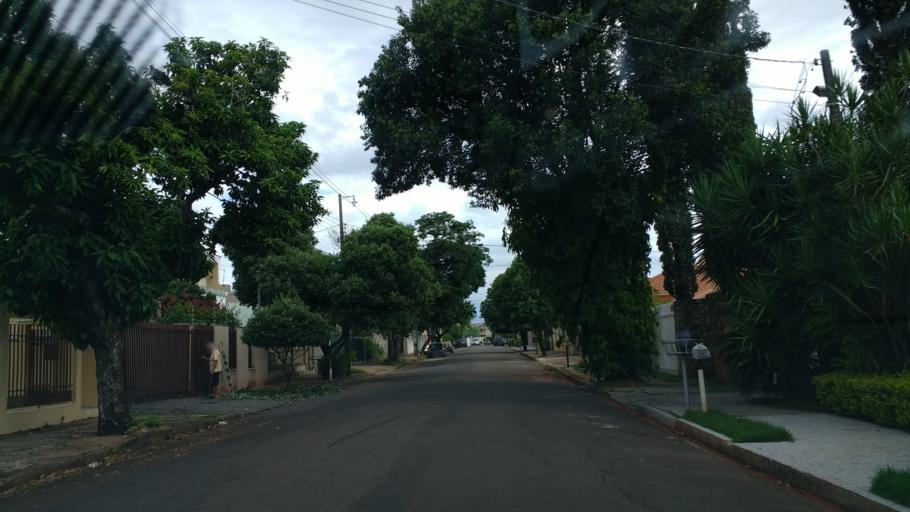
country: BR
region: Parana
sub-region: Londrina
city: Londrina
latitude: -23.3129
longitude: -51.1803
